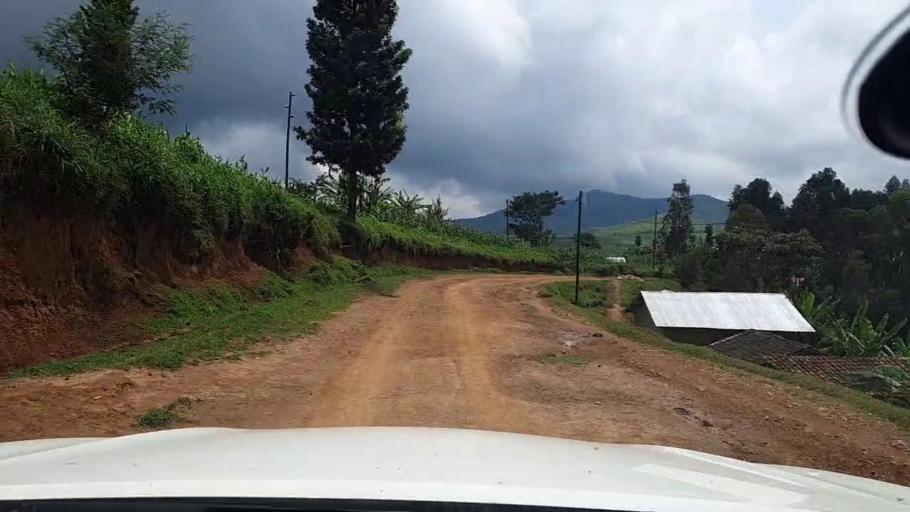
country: RW
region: Western Province
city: Kibuye
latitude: -2.1692
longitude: 29.4283
